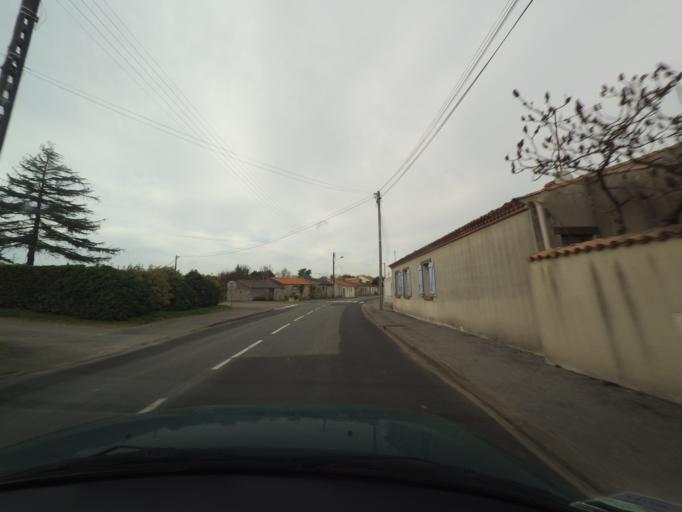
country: FR
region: Pays de la Loire
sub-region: Departement de la Loire-Atlantique
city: Chauve
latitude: 47.1325
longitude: -1.9713
